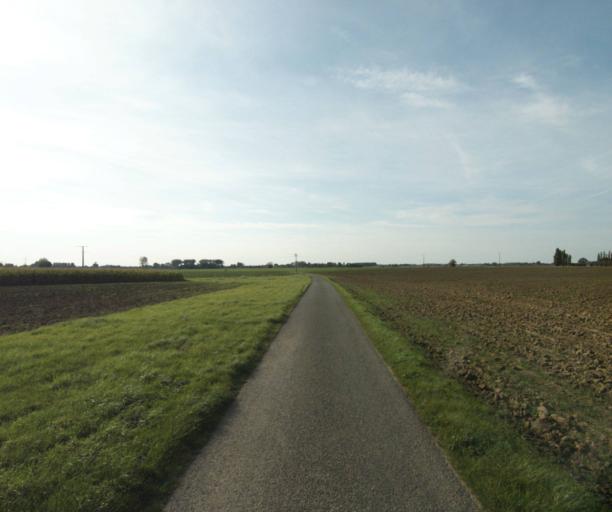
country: FR
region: Nord-Pas-de-Calais
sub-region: Departement du Nord
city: Fournes-en-Weppes
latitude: 50.5855
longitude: 2.8789
